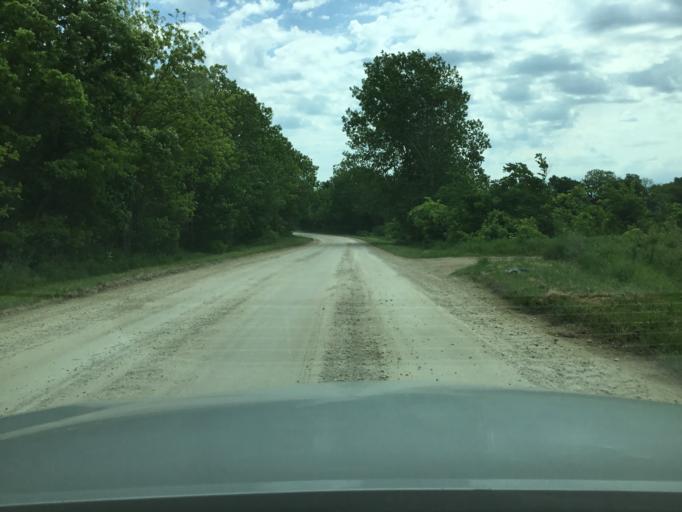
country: US
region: Kansas
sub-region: Montgomery County
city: Coffeyville
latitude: 37.0049
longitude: -95.5953
